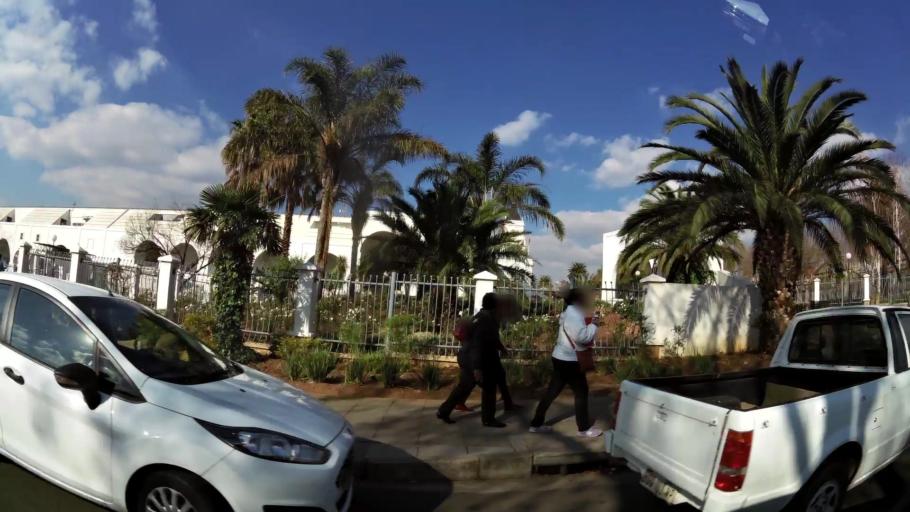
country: ZA
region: Gauteng
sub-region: West Rand District Municipality
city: Krugersdorp
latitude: -26.1008
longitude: 27.7714
